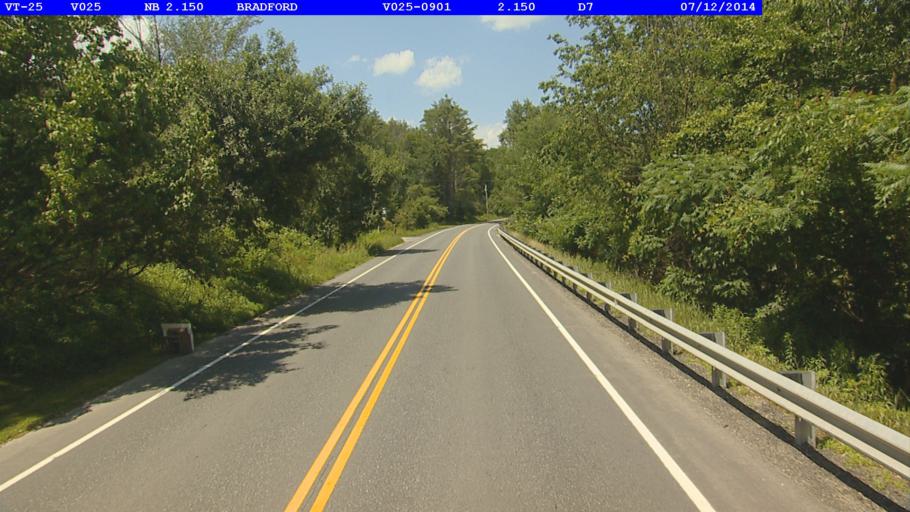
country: US
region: New Hampshire
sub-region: Grafton County
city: Orford
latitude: 43.9891
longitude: -72.1508
